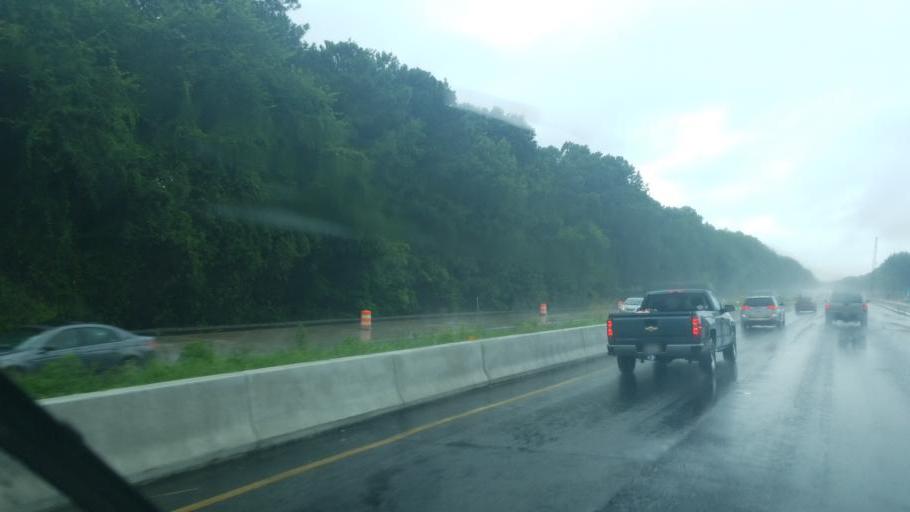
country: US
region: Virginia
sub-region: York County
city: Yorktown
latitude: 37.1449
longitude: -76.5323
